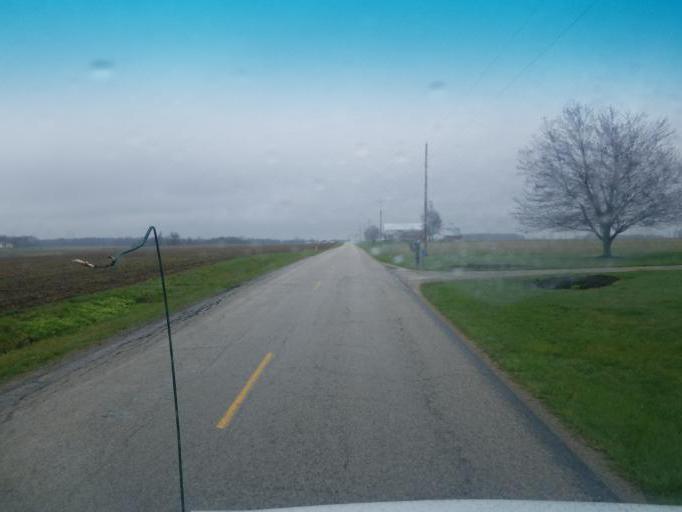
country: US
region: Ohio
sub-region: Crawford County
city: Bucyrus
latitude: 40.9649
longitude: -82.9857
